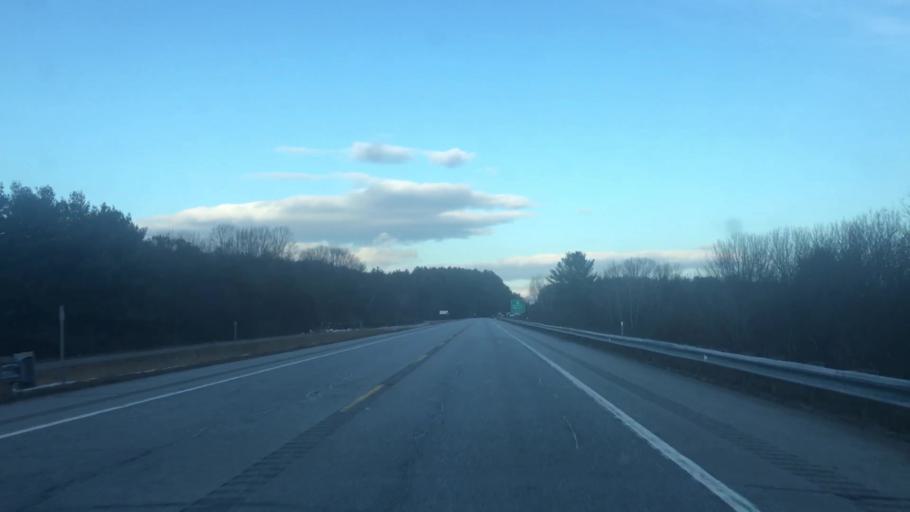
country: US
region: New Hampshire
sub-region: Merrimack County
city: Henniker
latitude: 43.1790
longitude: -71.8408
